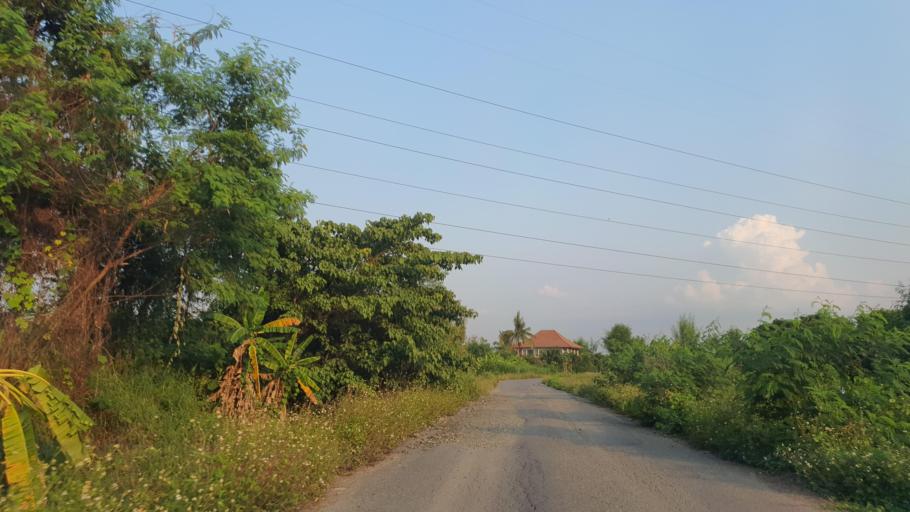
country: TH
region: Chiang Mai
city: Hang Dong
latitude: 18.6568
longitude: 98.9350
